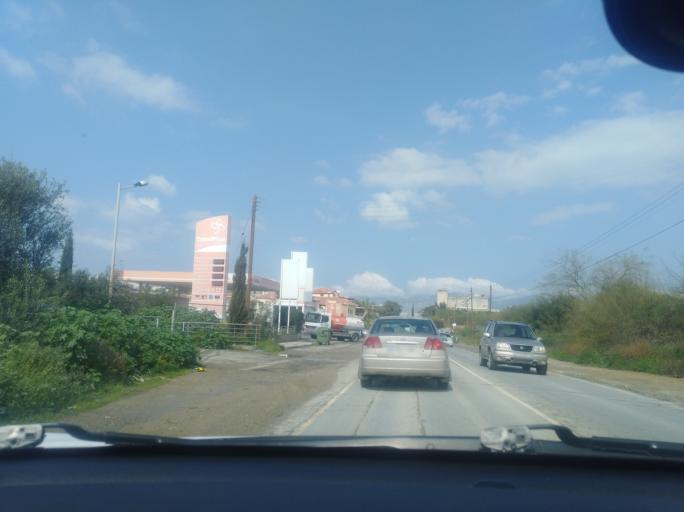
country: CY
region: Lefkosia
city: Nicosia
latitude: 35.1697
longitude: 33.3977
